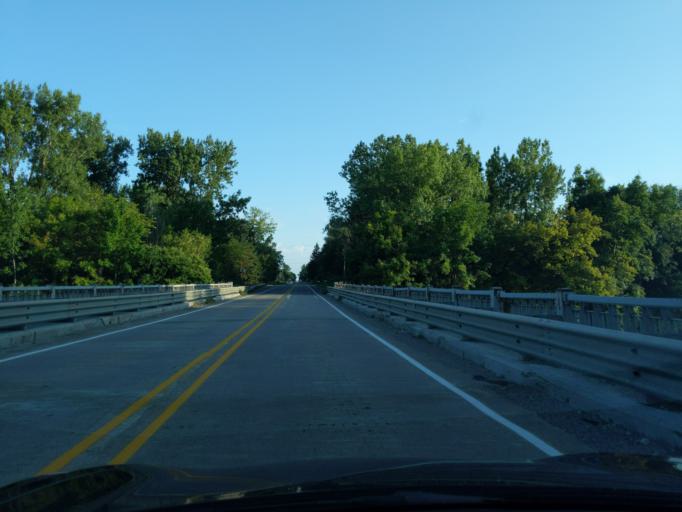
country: US
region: Michigan
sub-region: Midland County
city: Midland
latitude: 43.5645
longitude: -84.3696
